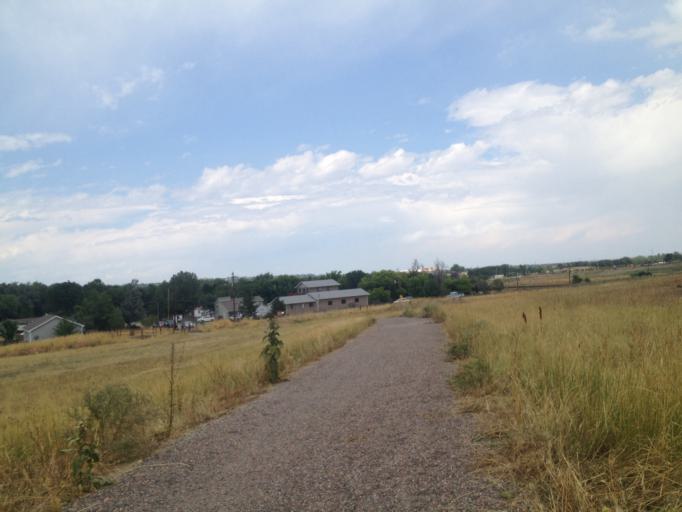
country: US
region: Colorado
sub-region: Boulder County
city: Superior
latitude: 39.9481
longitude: -105.1698
